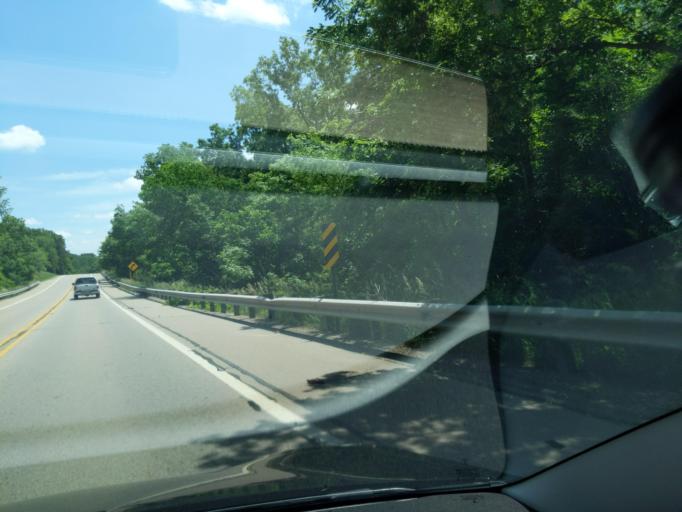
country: US
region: Michigan
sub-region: Ionia County
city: Portland
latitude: 43.0020
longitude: -84.9325
